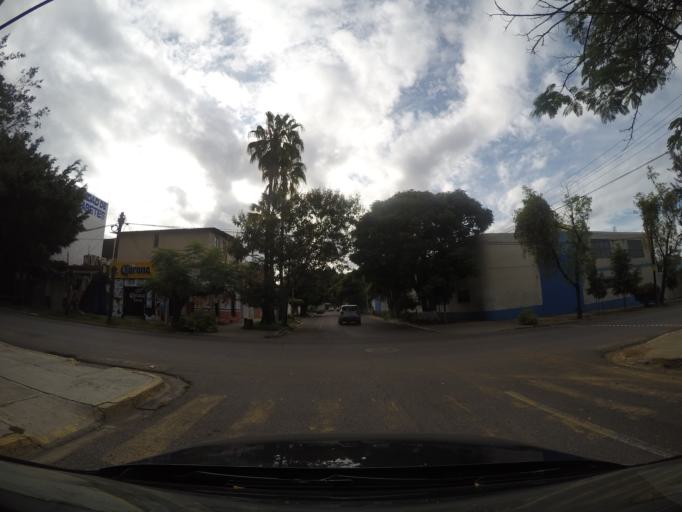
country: MX
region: Oaxaca
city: Oaxaca de Juarez
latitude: 17.0766
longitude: -96.7172
